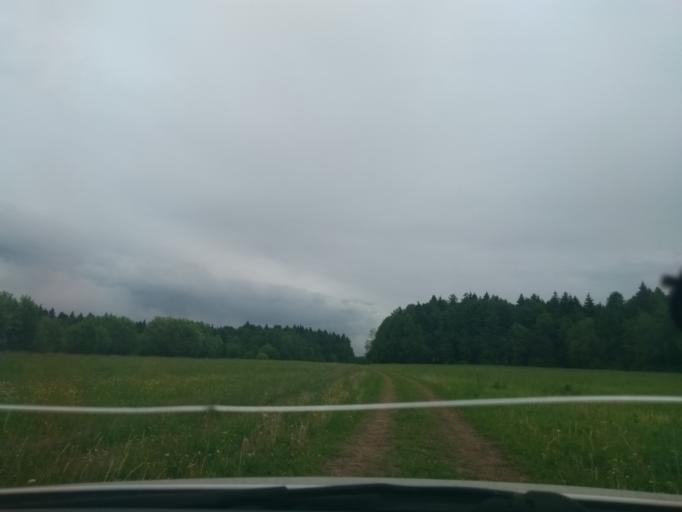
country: RU
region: Perm
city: Ferma
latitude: 57.9827
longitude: 56.3327
